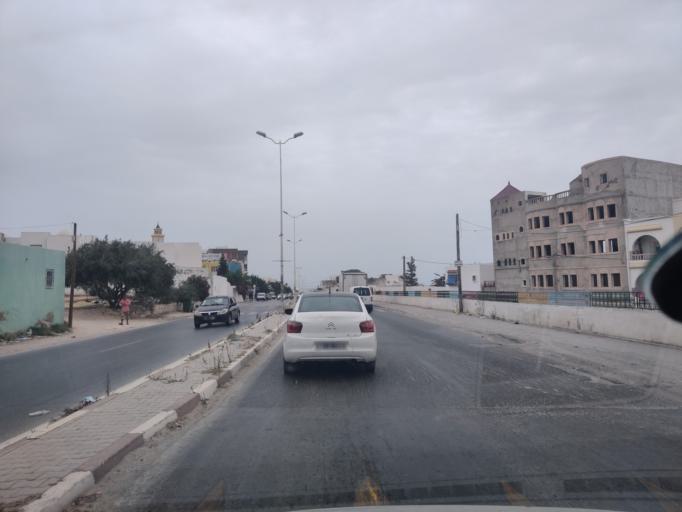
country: TN
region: Nabul
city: Al Hammamat
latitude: 36.4083
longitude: 10.6301
